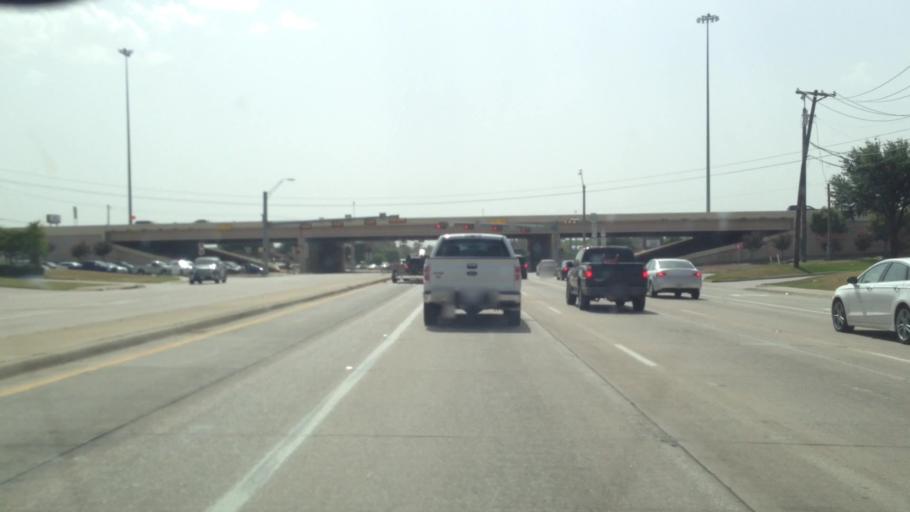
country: US
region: Texas
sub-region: Collin County
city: McKinney
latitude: 33.2167
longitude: -96.6346
